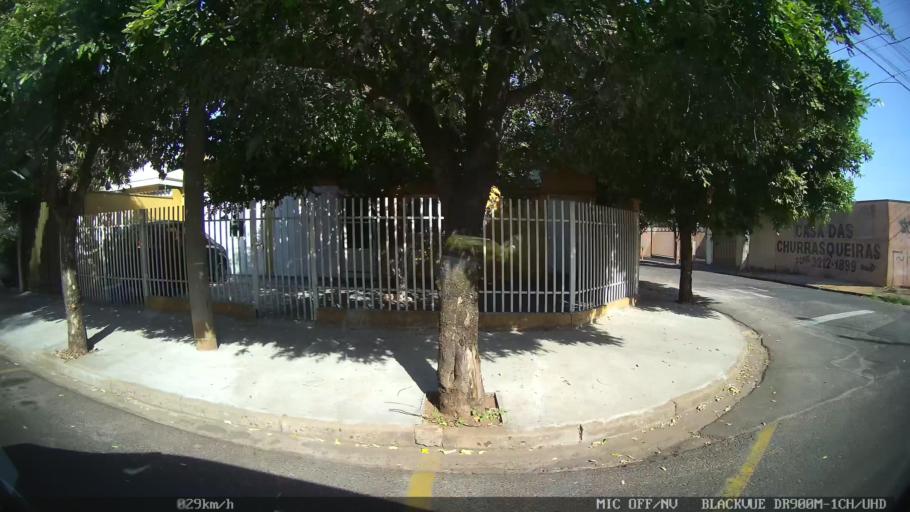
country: BR
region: Sao Paulo
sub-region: Sao Jose Do Rio Preto
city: Sao Jose do Rio Preto
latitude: -20.8083
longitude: -49.3948
